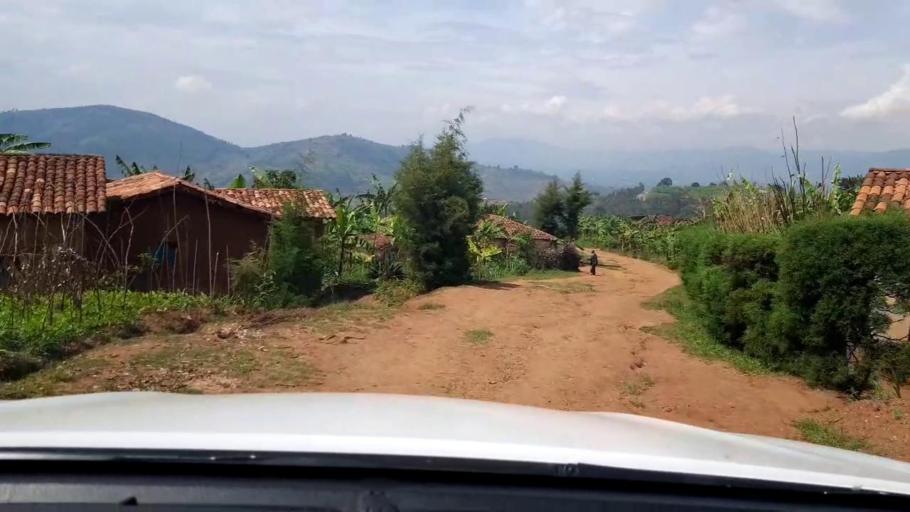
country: RW
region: Southern Province
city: Gitarama
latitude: -2.0573
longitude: 29.6693
